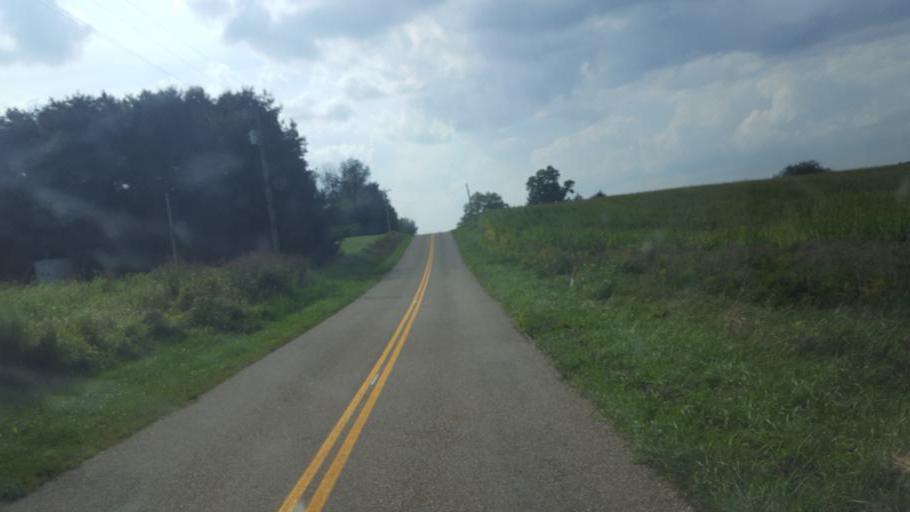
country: US
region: Ohio
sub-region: Knox County
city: Gambier
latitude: 40.3366
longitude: -82.3655
